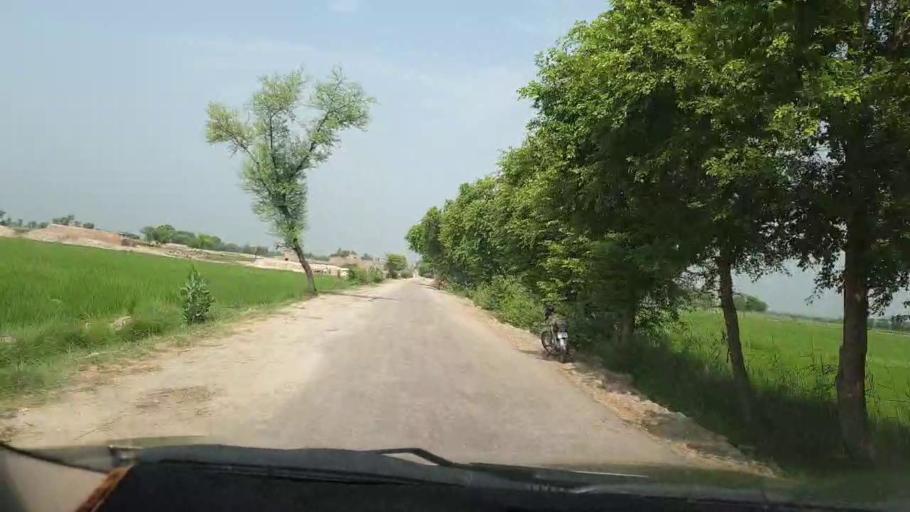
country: PK
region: Sindh
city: Goth Garelo
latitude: 27.4843
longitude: 68.0438
